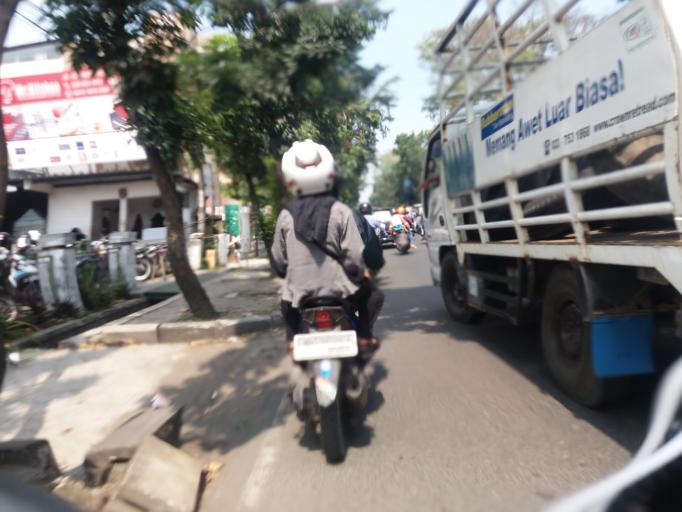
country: ID
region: West Java
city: Bandung
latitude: -6.9115
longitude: 107.5781
